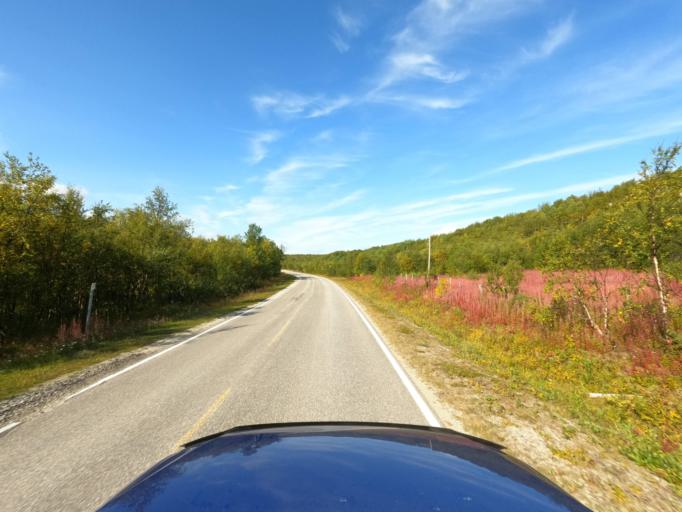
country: NO
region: Finnmark Fylke
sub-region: Porsanger
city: Lakselv
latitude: 69.7616
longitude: 25.2025
